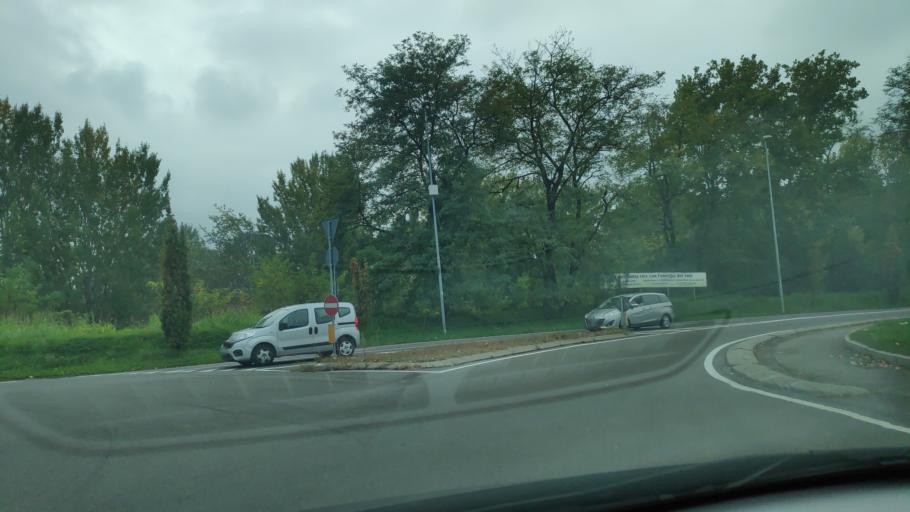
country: IT
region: Lombardy
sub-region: Provincia di Varese
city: Castellanza
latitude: 45.6075
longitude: 8.9090
